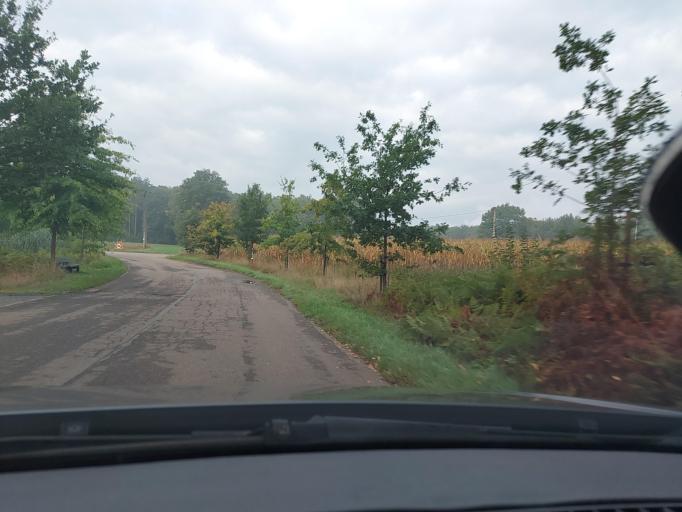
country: BE
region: Flanders
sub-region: Provincie Antwerpen
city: Laakdal
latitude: 51.1045
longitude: 5.0323
